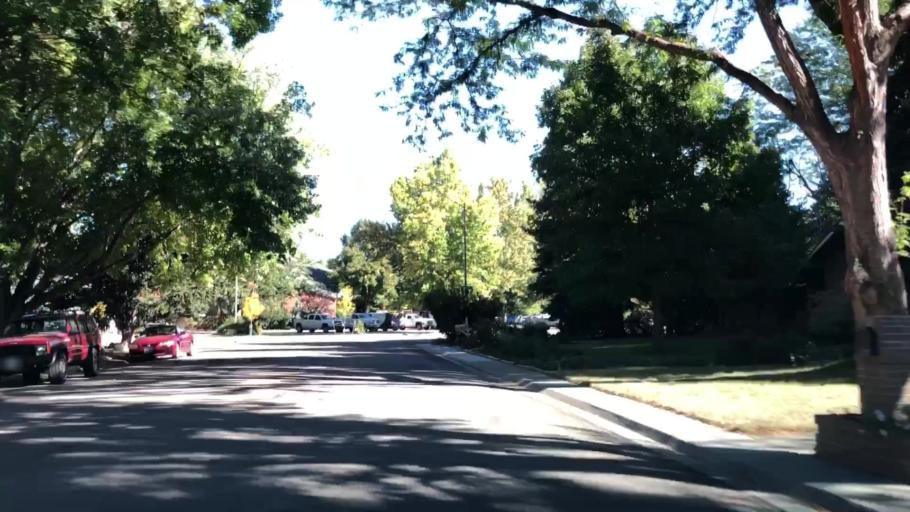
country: US
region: Colorado
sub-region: Larimer County
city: Fort Collins
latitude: 40.5579
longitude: -105.0573
